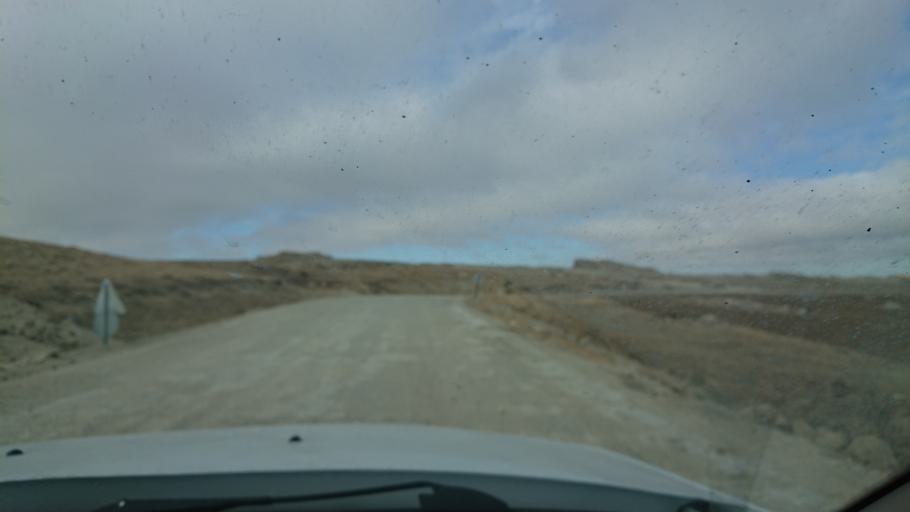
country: TR
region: Aksaray
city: Ortakoy
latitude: 38.7796
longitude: 34.0063
